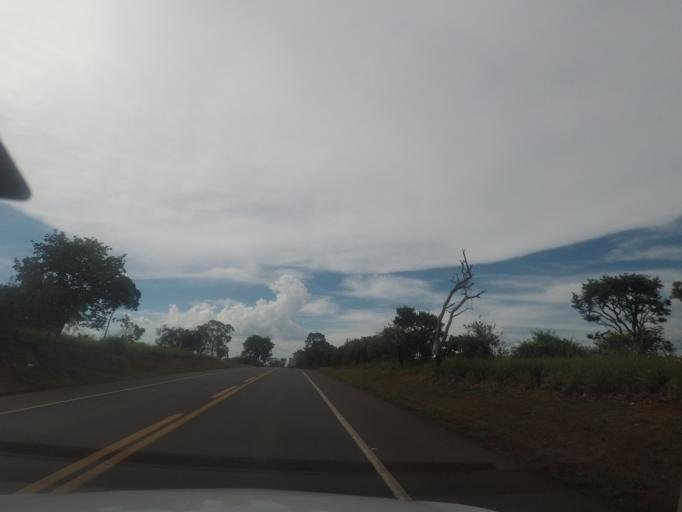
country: BR
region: Minas Gerais
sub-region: Prata
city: Prata
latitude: -19.2529
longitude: -48.9255
